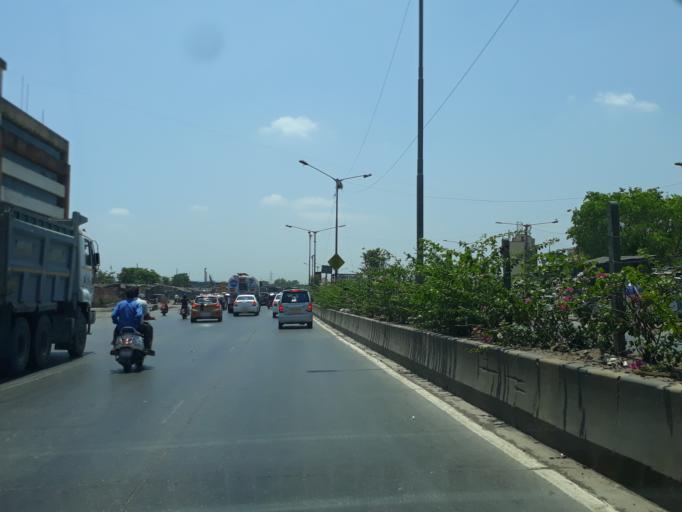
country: IN
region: Maharashtra
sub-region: Mumbai Suburban
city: Mumbai
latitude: 19.0565
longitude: 72.9301
